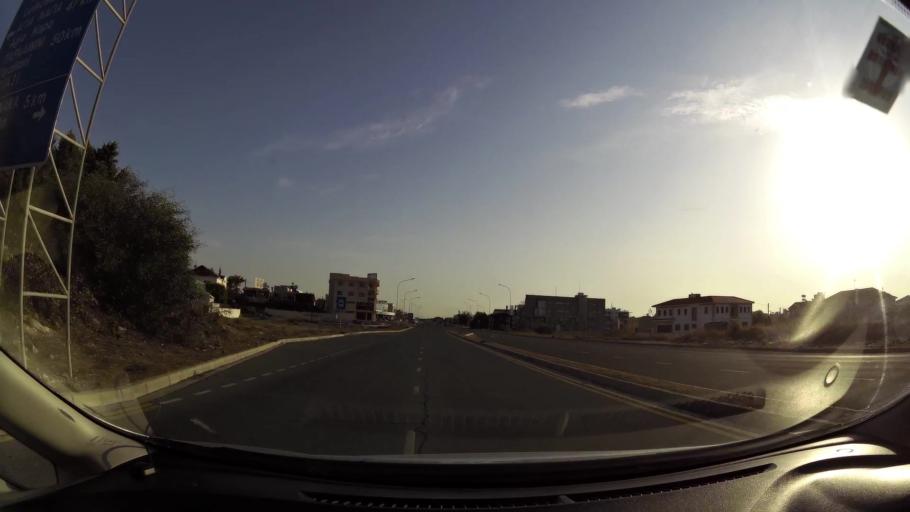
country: CY
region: Larnaka
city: Aradippou
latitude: 34.9317
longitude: 33.5940
